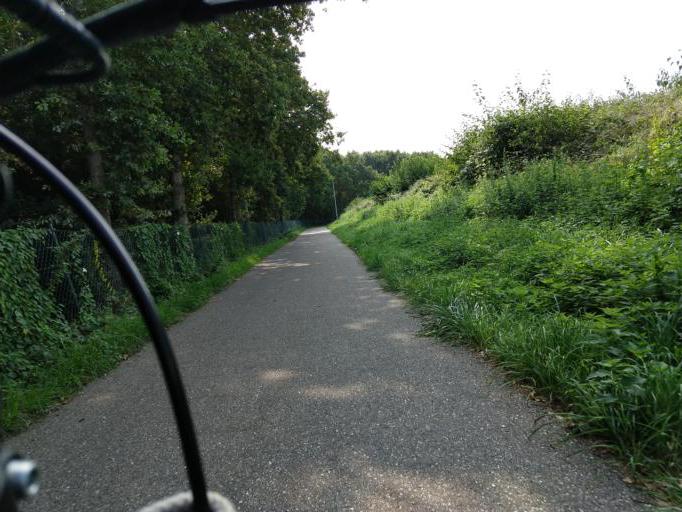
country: NL
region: Zeeland
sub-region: Gemeente Goes
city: Goes
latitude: 51.5457
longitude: 3.8631
